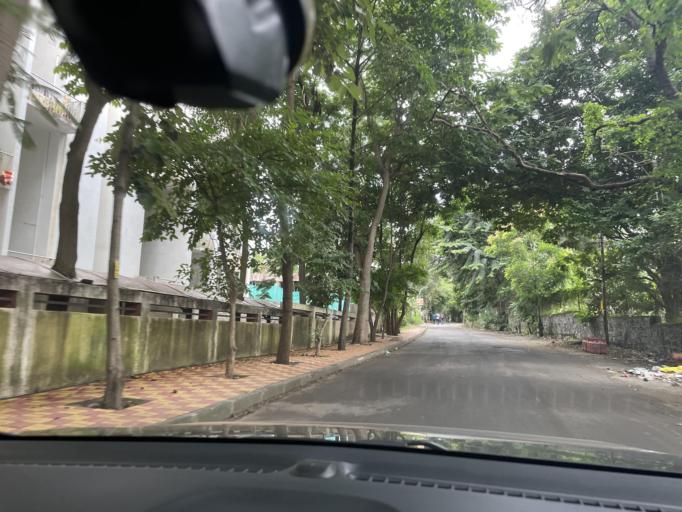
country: IN
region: Maharashtra
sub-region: Pune Division
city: Kharakvasla
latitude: 18.5144
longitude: 73.7790
